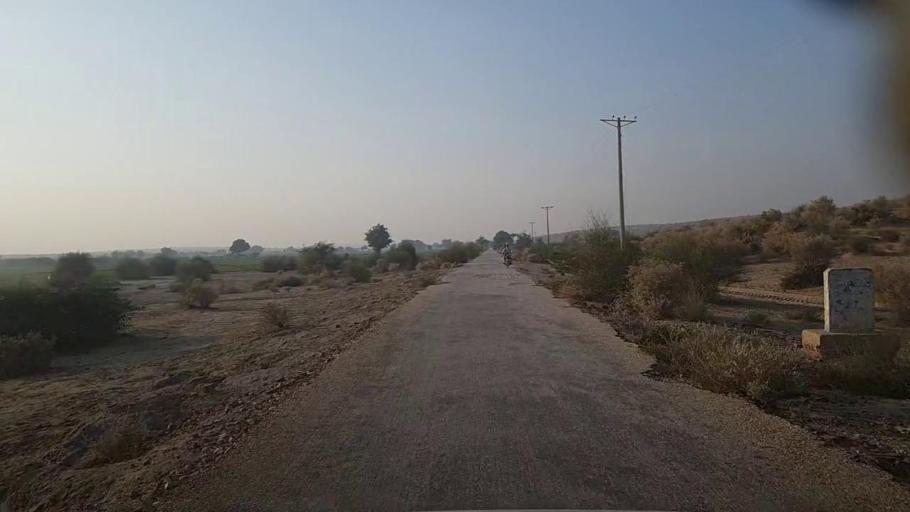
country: PK
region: Sindh
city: Pad Idan
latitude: 26.7159
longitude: 68.4635
